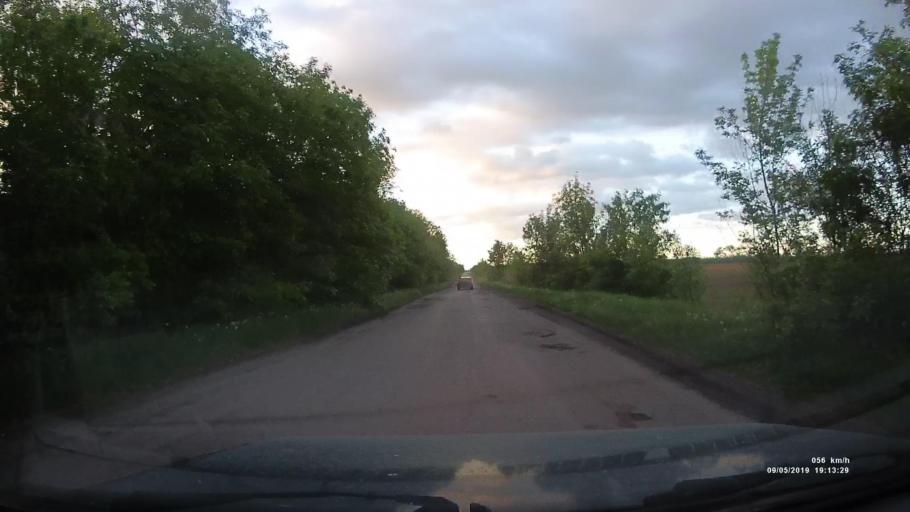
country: RU
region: Krasnodarskiy
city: Kanelovskaya
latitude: 46.7511
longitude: 39.2138
